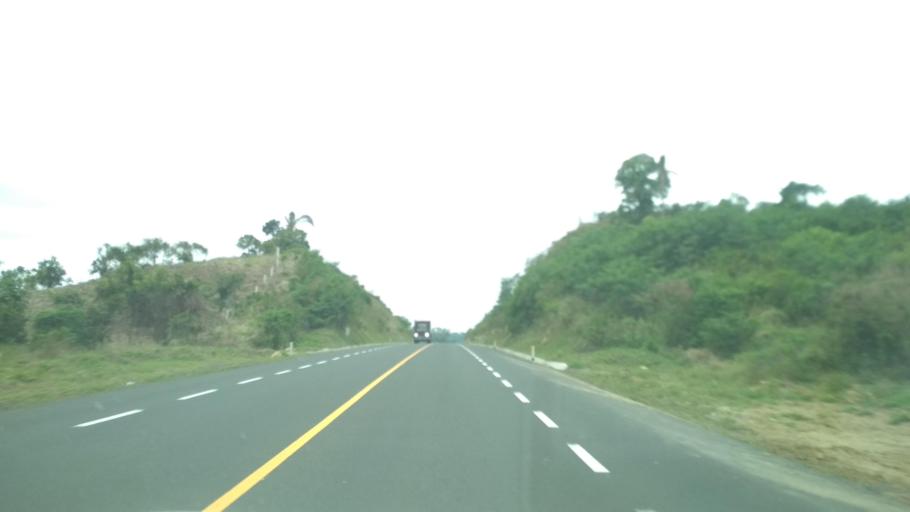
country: MX
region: Veracruz
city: Gutierrez Zamora
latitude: 20.3044
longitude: -97.0947
